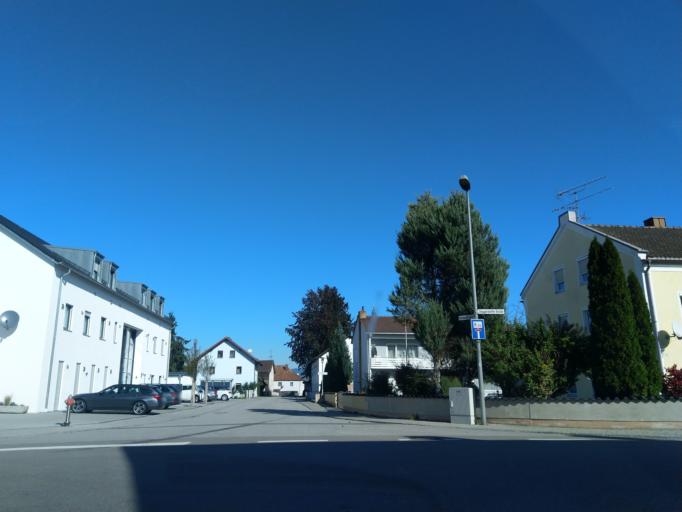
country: DE
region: Bavaria
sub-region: Lower Bavaria
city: Stephansposching
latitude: 48.8166
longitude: 12.8025
